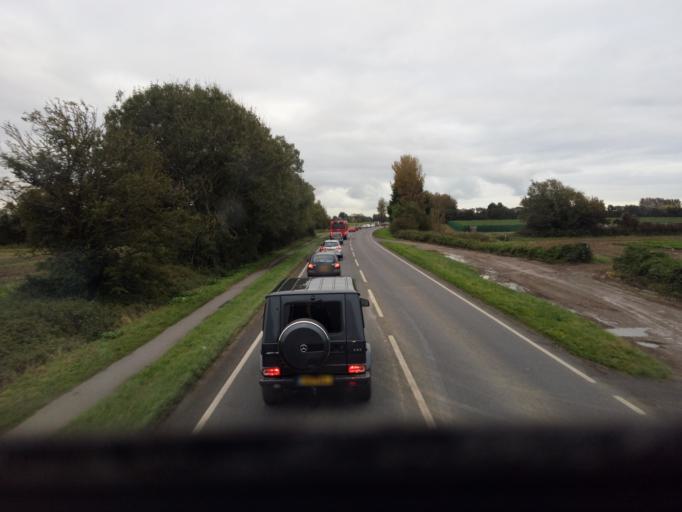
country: GB
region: England
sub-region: West Sussex
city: Boxgrove
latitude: 50.8224
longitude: -0.7248
